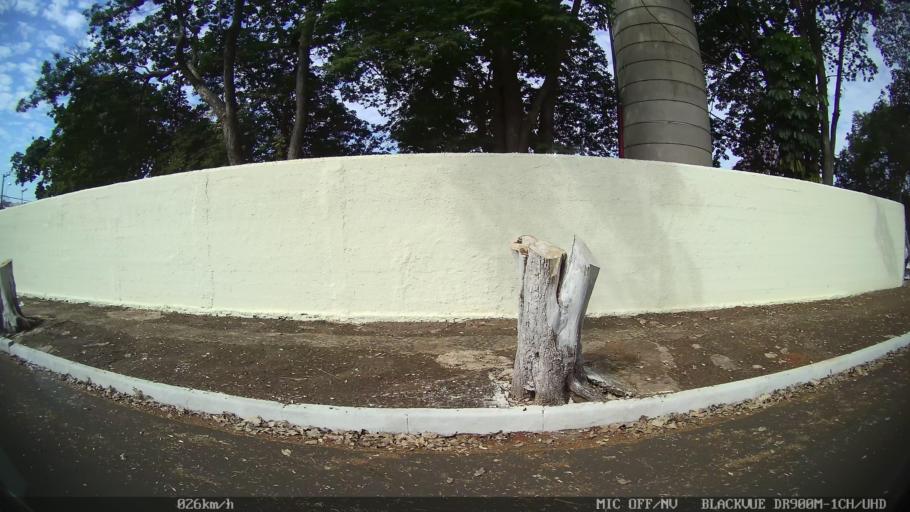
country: BR
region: Sao Paulo
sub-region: Santa Barbara D'Oeste
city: Santa Barbara d'Oeste
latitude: -22.7493
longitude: -47.4250
